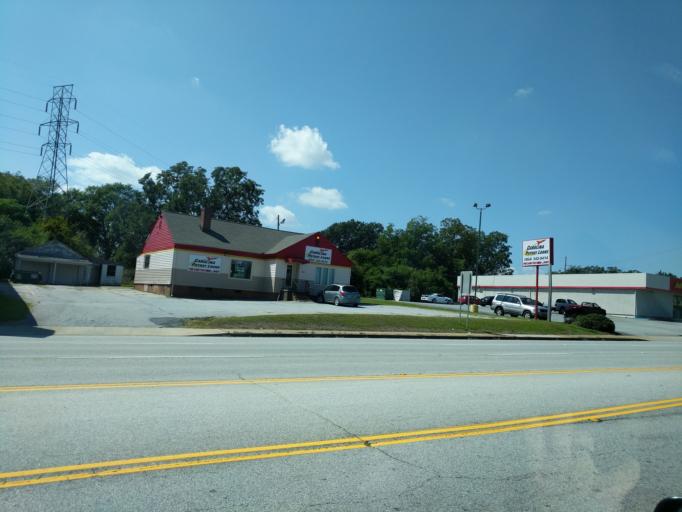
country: US
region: South Carolina
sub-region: Spartanburg County
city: Saxon
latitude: 34.9739
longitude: -81.9572
